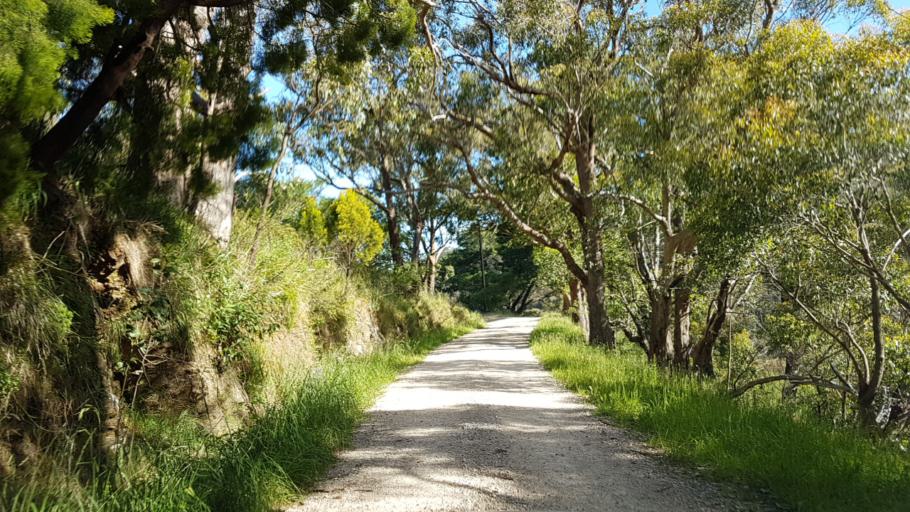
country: AU
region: South Australia
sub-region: Adelaide Hills
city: Adelaide Hills
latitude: -34.9120
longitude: 138.7597
